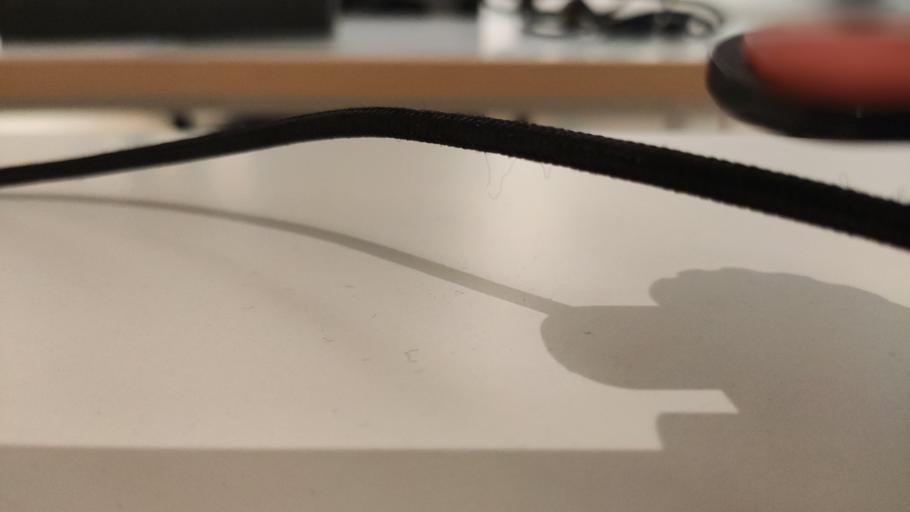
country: RU
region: Moskovskaya
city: Ruza
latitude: 55.6686
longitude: 36.2631
